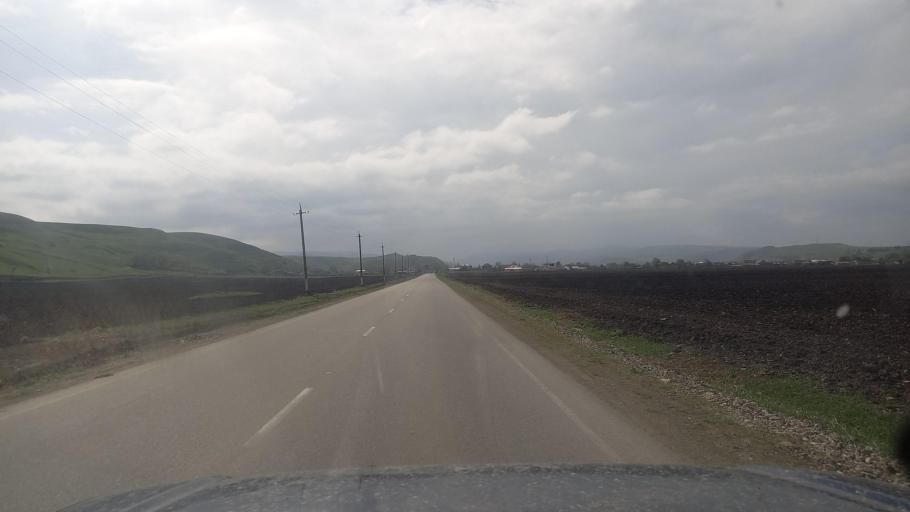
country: RU
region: Kabardino-Balkariya
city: Kamennomostskoye
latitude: 43.7283
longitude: 43.0859
